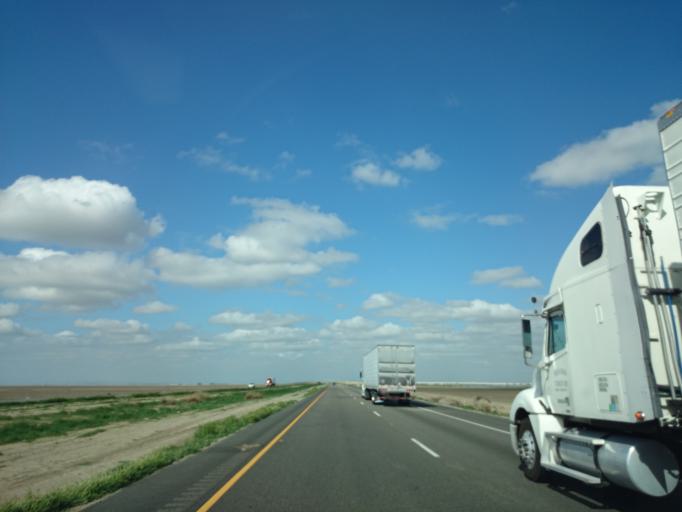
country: US
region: California
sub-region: Kern County
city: Greenfield
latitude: 35.1401
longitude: -119.0868
